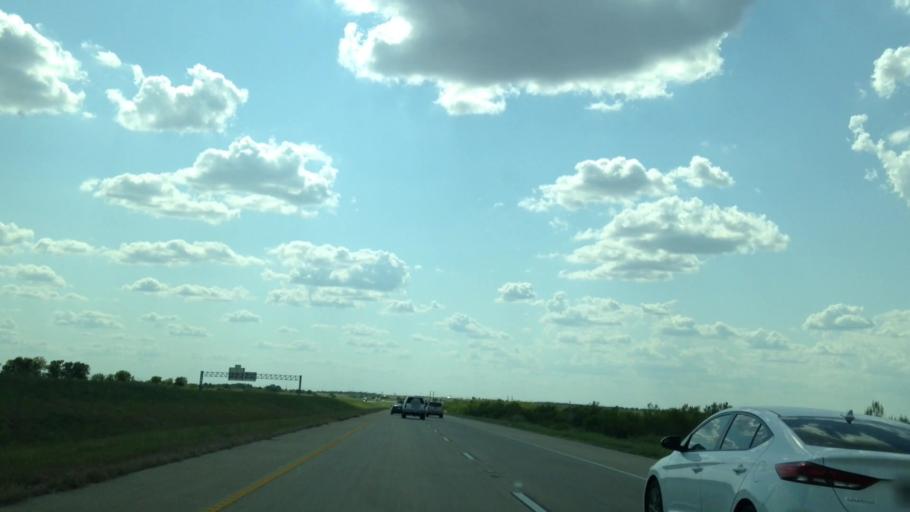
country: US
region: Texas
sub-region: Travis County
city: Onion Creek
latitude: 30.0820
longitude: -97.7156
